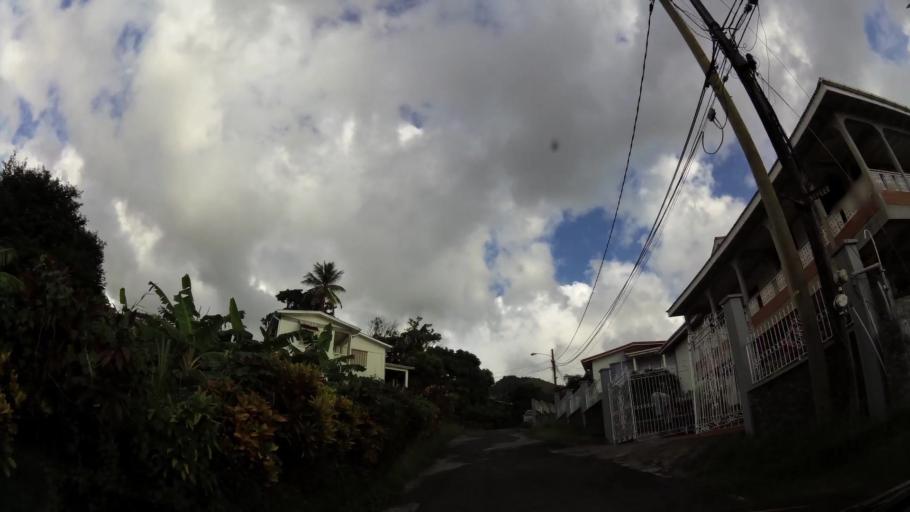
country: DM
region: Saint Paul
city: Mahaut
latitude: 15.3386
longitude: -61.3879
